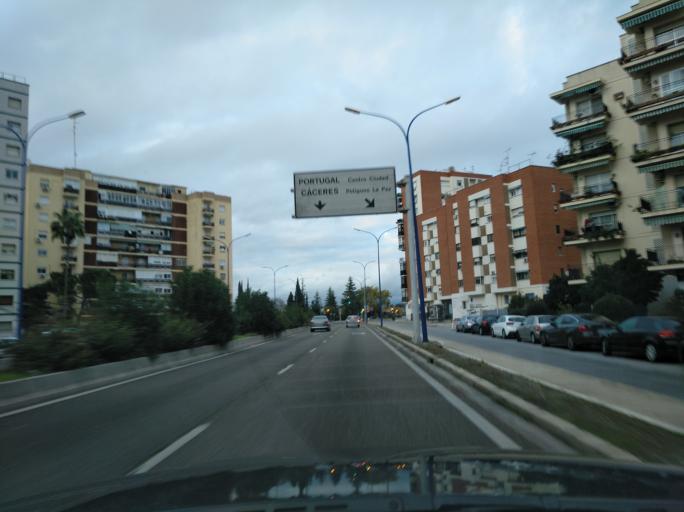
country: ES
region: Extremadura
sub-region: Provincia de Badajoz
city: Badajoz
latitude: 38.8764
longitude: -6.9811
